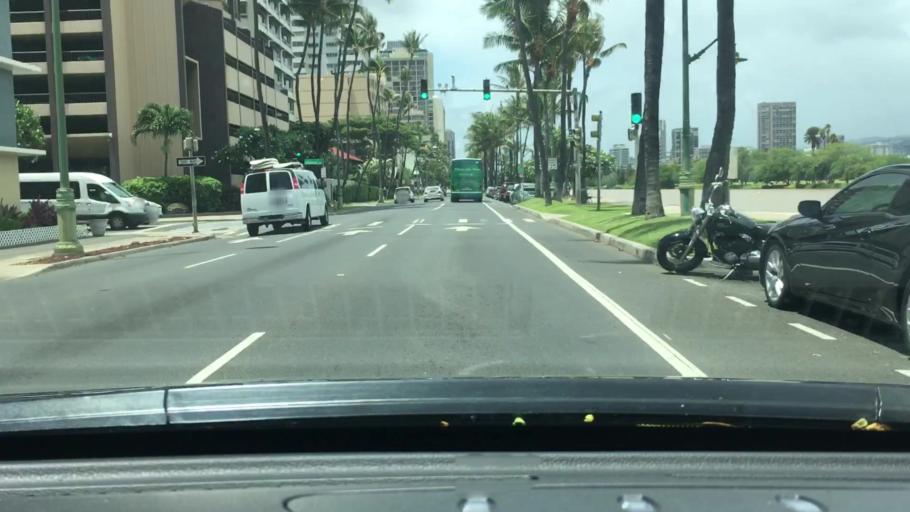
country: US
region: Hawaii
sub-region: Honolulu County
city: Honolulu
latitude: 21.2769
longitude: -157.8203
